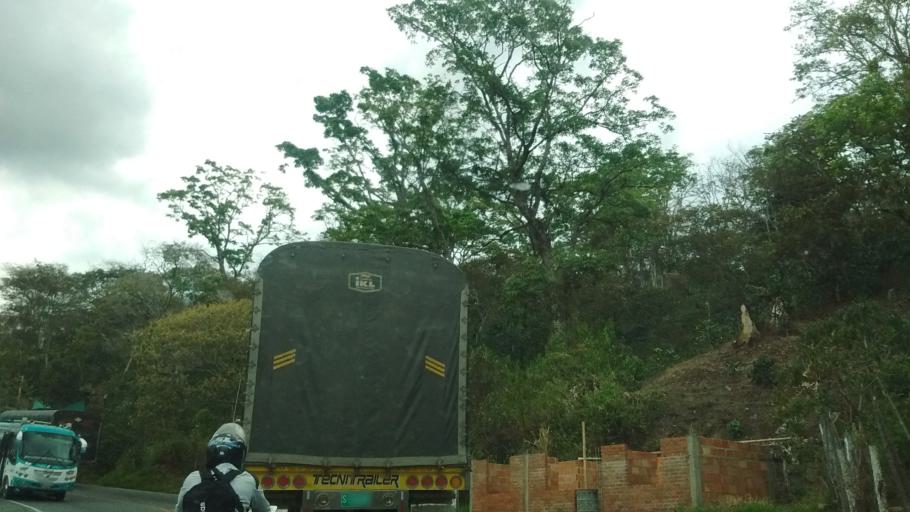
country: CO
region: Cauca
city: Rosas
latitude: 2.2768
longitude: -76.7221
